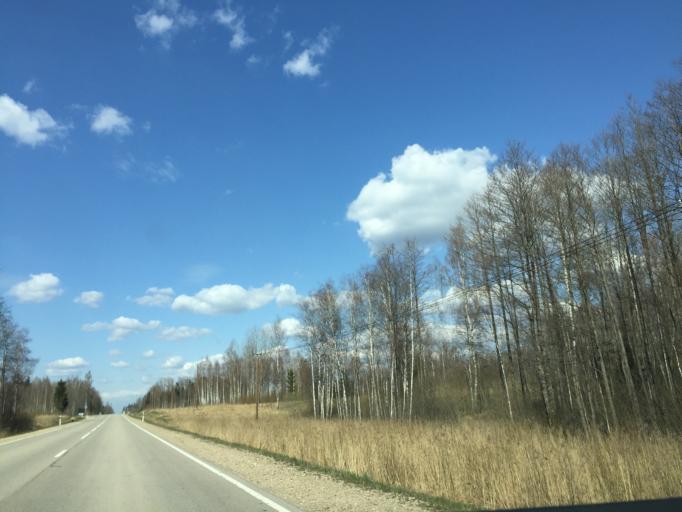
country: LV
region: Skriveri
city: Skriveri
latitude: 56.7987
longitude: 25.1594
